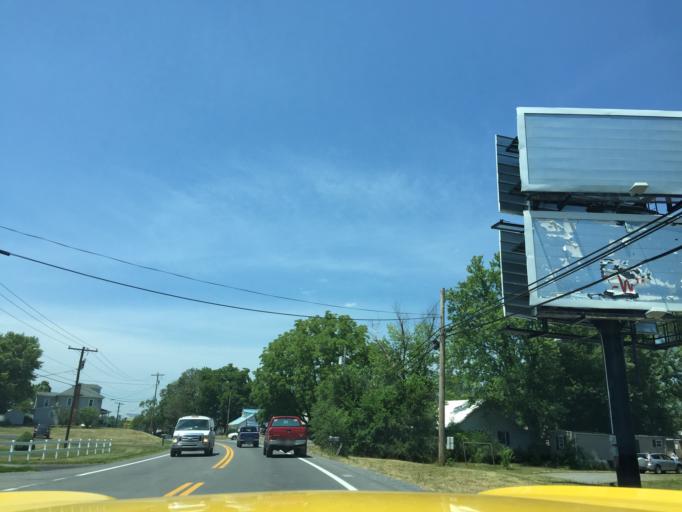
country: US
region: West Virginia
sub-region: Berkeley County
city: Inwood
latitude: 39.3560
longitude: -78.0346
